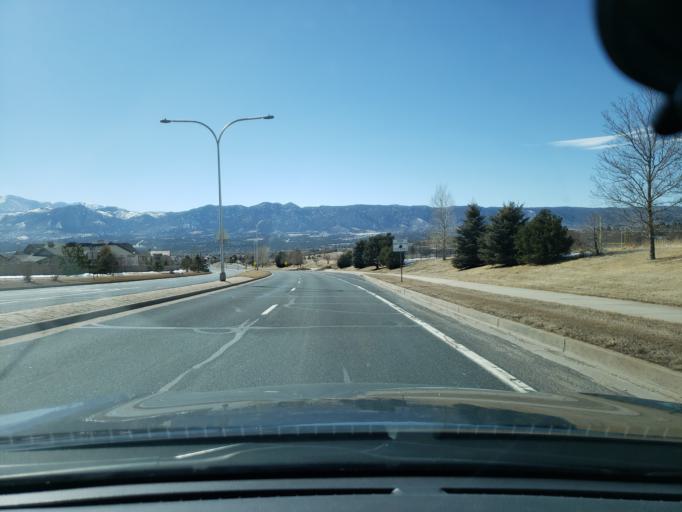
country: US
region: Colorado
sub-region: El Paso County
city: Gleneagle
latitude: 39.0300
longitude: -104.7910
